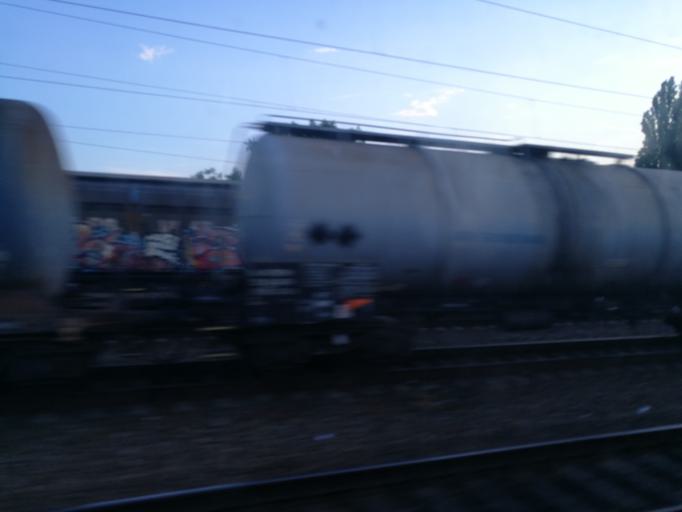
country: RO
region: Ilfov
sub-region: Comuna Chitila
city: Chitila
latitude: 44.5029
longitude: 25.9827
